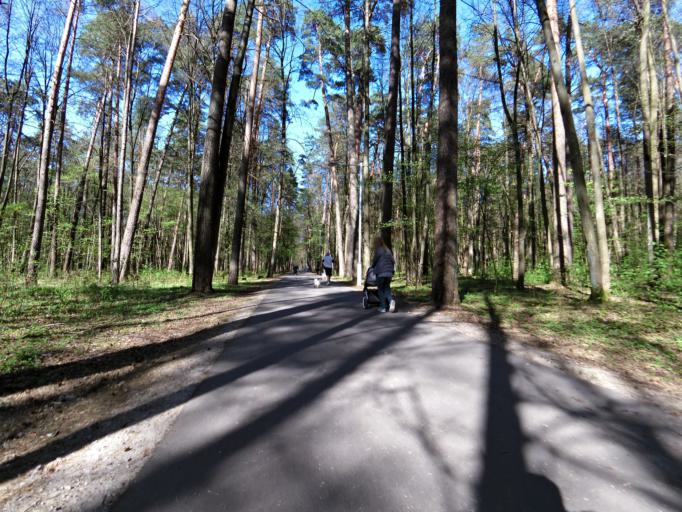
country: LT
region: Vilnius County
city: Vilkpede
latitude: 54.6853
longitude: 25.2371
